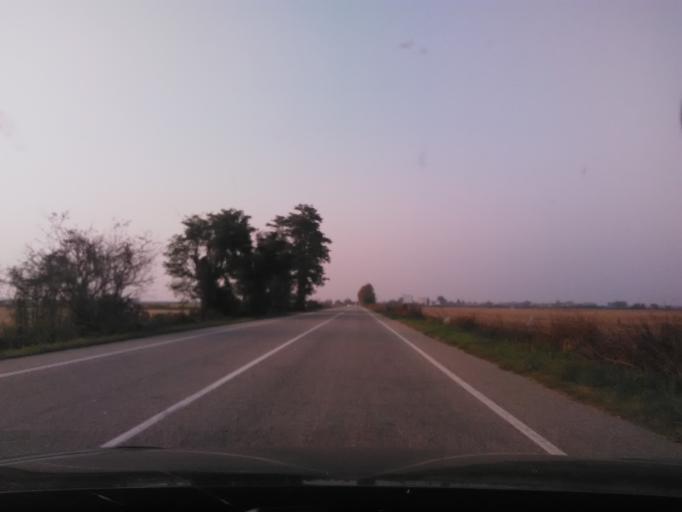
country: IT
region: Piedmont
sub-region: Provincia di Vercelli
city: Stroppiana
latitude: 45.2104
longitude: 8.4591
